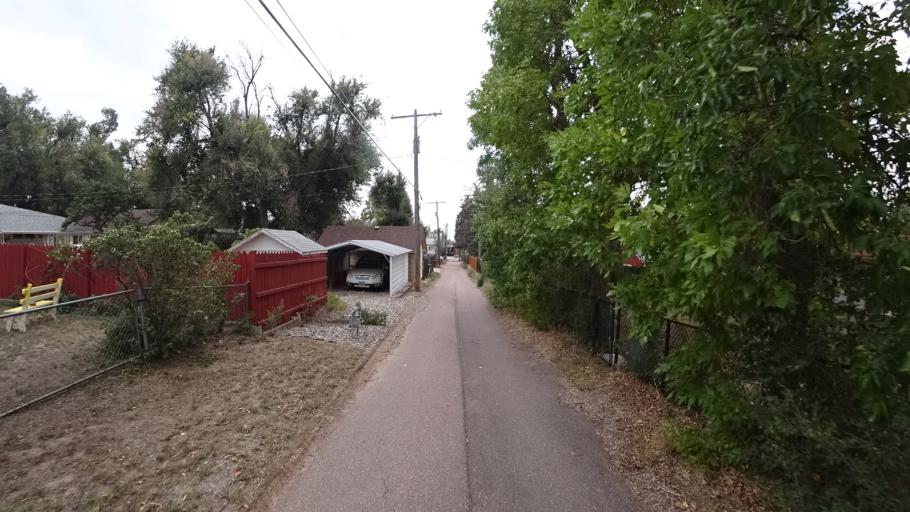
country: US
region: Colorado
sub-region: El Paso County
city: Colorado Springs
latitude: 38.8475
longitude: -104.7921
